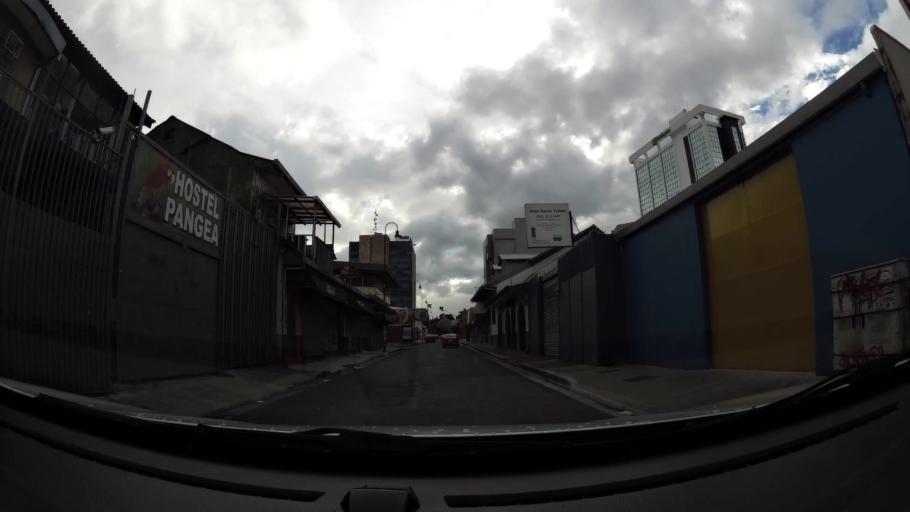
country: CR
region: San Jose
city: San Jose
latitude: 9.9371
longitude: -84.0766
